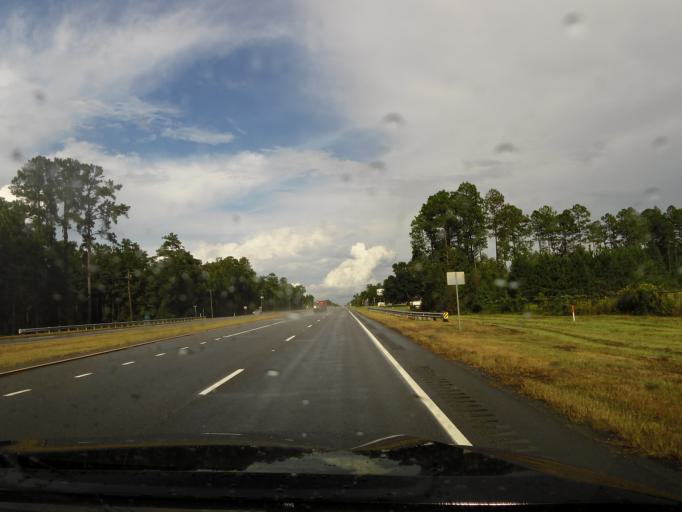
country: US
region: Georgia
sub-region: Liberty County
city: Walthourville
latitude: 31.7523
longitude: -81.6726
